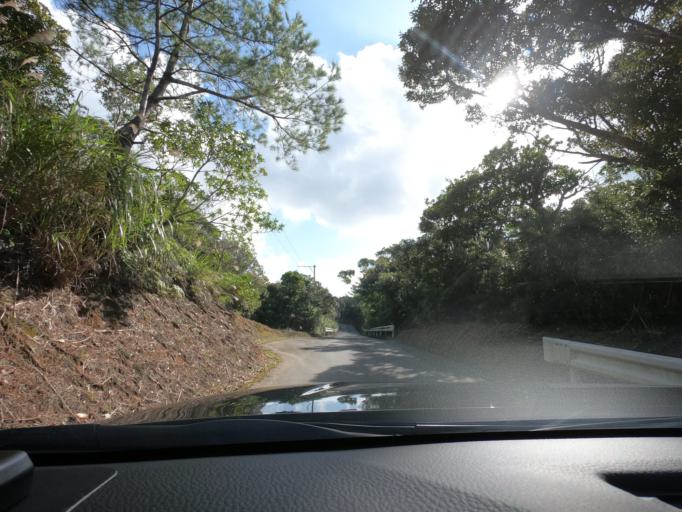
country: JP
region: Okinawa
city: Nago
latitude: 26.7551
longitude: 128.2062
